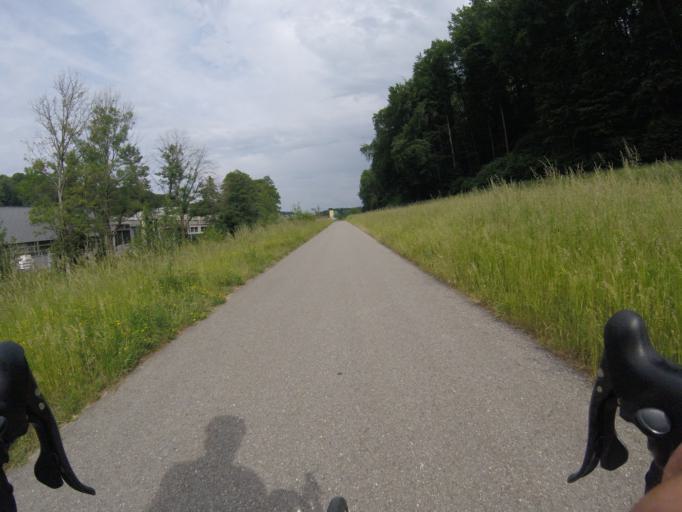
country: CH
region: Bern
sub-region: Seeland District
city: Lyss
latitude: 47.0665
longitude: 7.3220
